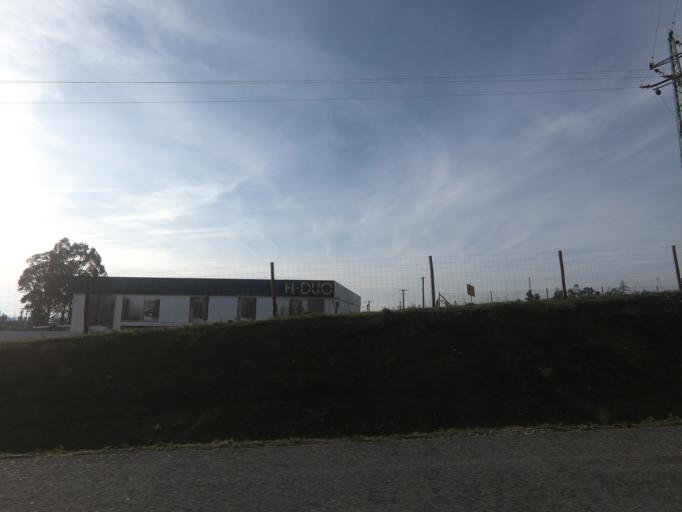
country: PT
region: Viseu
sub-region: Concelho de Tondela
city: Tondela
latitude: 40.4847
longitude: -8.0867
